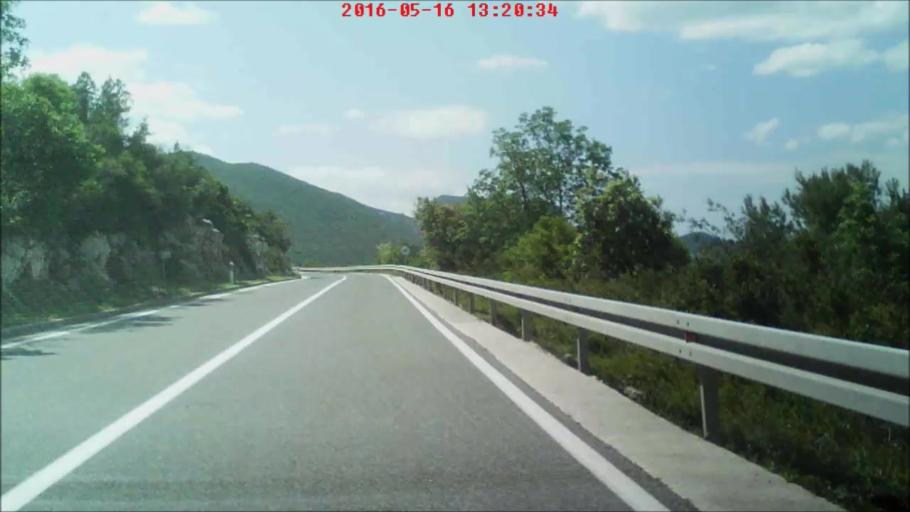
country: HR
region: Dubrovacko-Neretvanska
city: Ston
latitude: 42.8316
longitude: 17.7441
